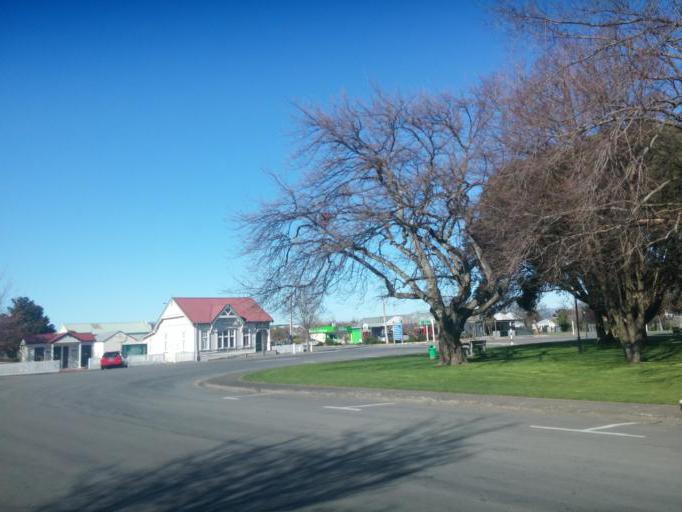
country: NZ
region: Wellington
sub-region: South Wairarapa District
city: Waipawa
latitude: -41.2183
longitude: 175.4601
